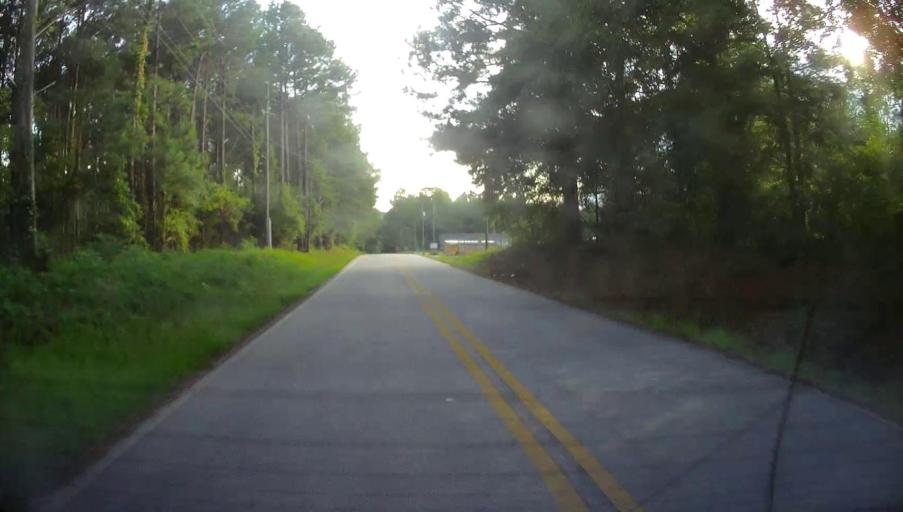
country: US
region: Georgia
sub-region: Monroe County
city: Forsyth
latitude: 33.0187
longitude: -83.9563
